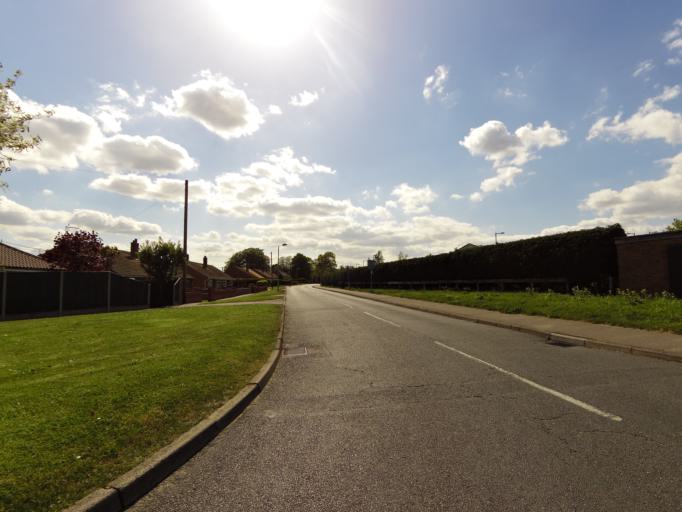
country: GB
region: England
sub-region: Suffolk
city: Kessingland
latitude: 52.4539
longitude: 1.6979
